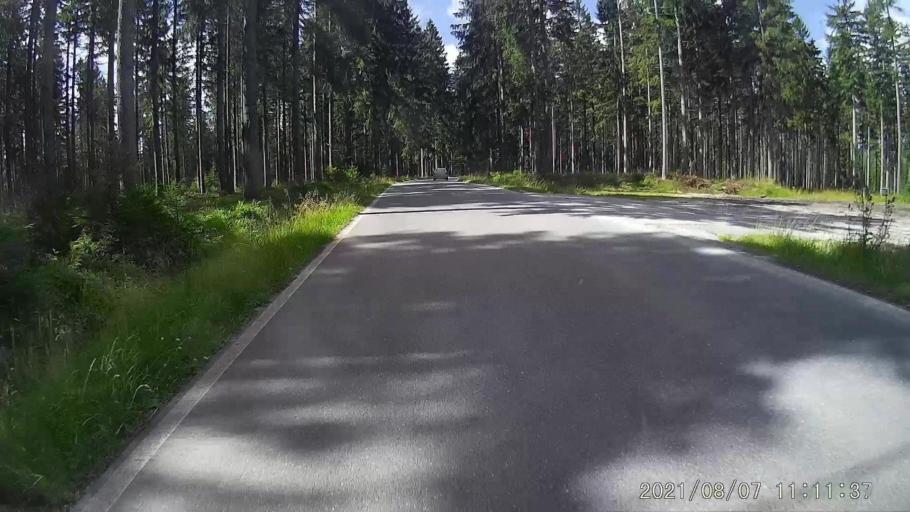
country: CZ
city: Rokytnice v Orlickych Horach
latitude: 50.2759
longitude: 16.5035
